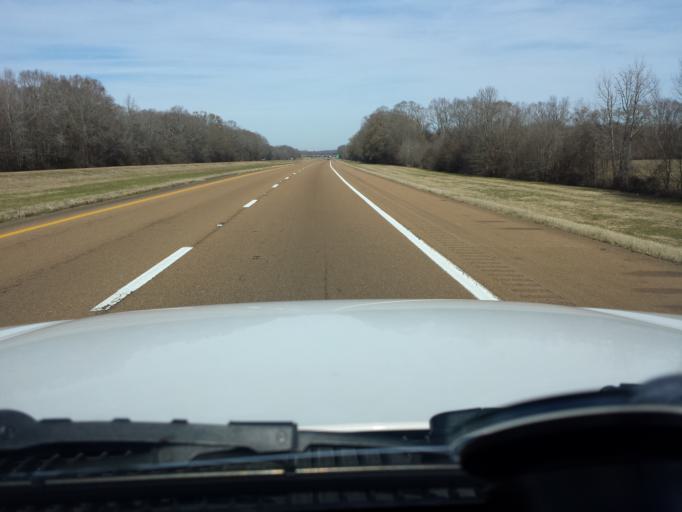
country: US
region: Mississippi
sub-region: Madison County
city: Canton
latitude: 32.6522
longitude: -90.0622
